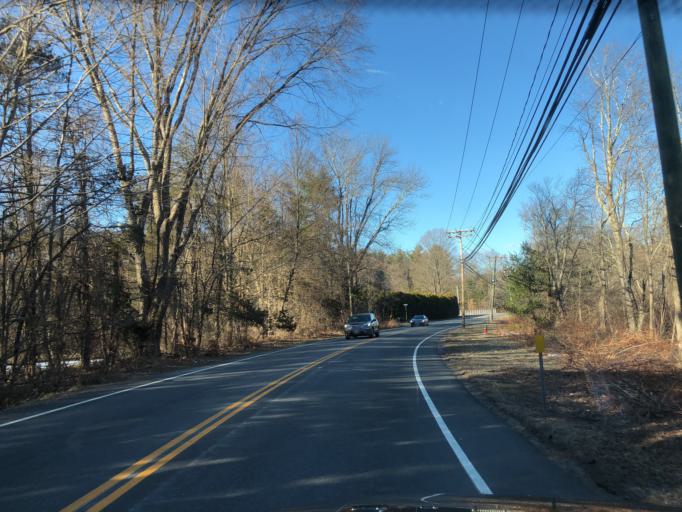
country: US
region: Connecticut
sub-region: Hartford County
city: Collinsville
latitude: 41.7924
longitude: -72.8930
